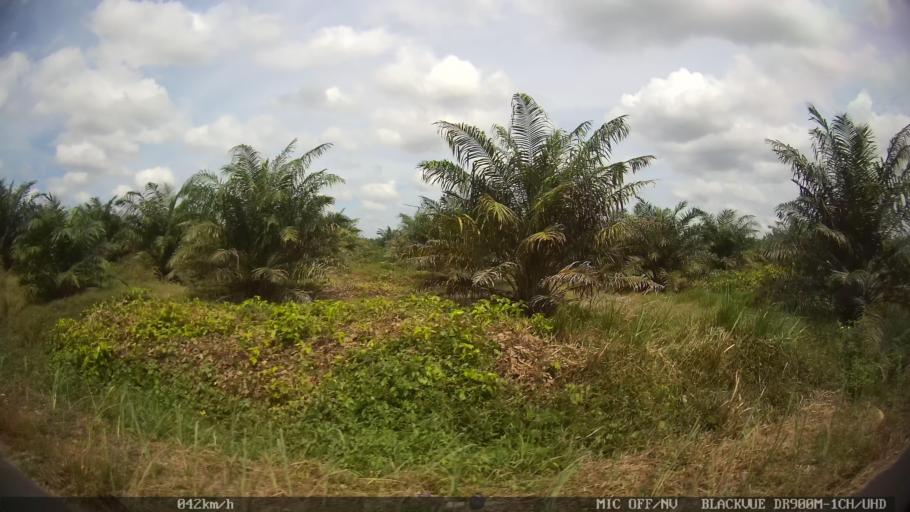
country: ID
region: North Sumatra
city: Percut
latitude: 3.5860
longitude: 98.8410
